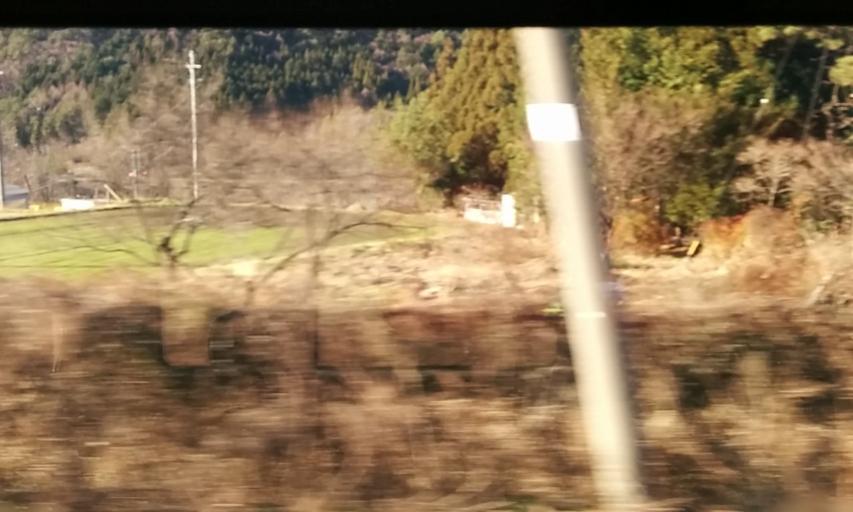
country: JP
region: Nagano
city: Ina
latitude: 35.8626
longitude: 137.7252
